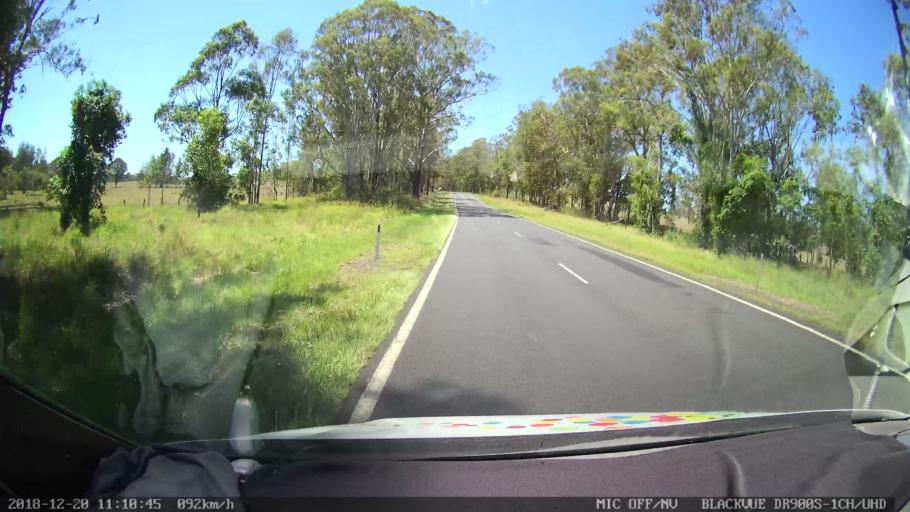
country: AU
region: New South Wales
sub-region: Richmond Valley
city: Casino
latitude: -28.9532
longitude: 153.0103
